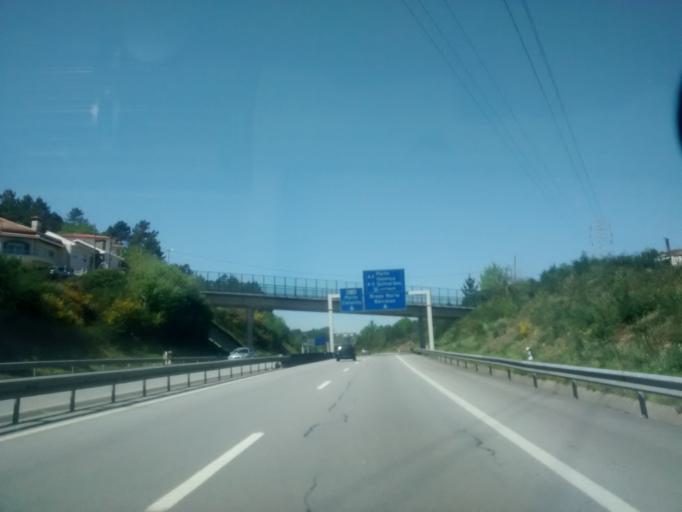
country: PT
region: Braga
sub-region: Braga
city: Braga
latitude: 41.5184
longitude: -8.4361
